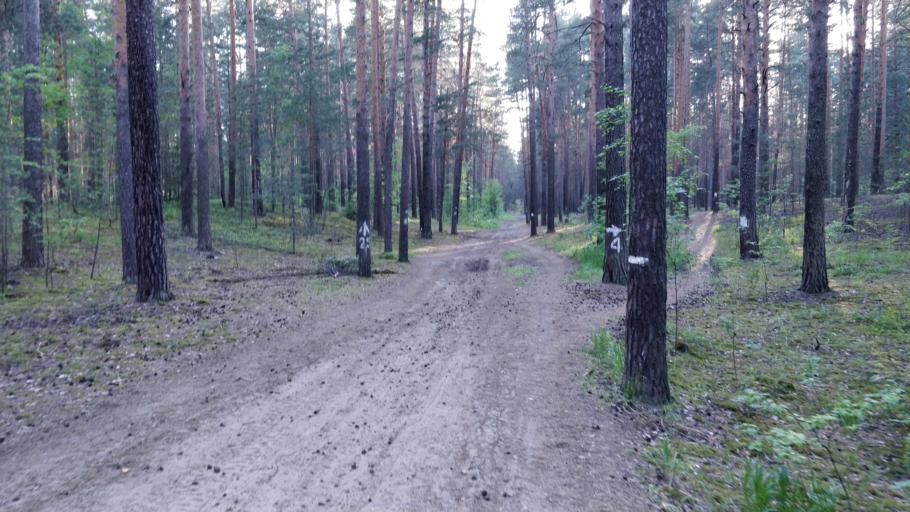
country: RU
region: Perm
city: Perm
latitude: 58.0658
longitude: 56.2923
